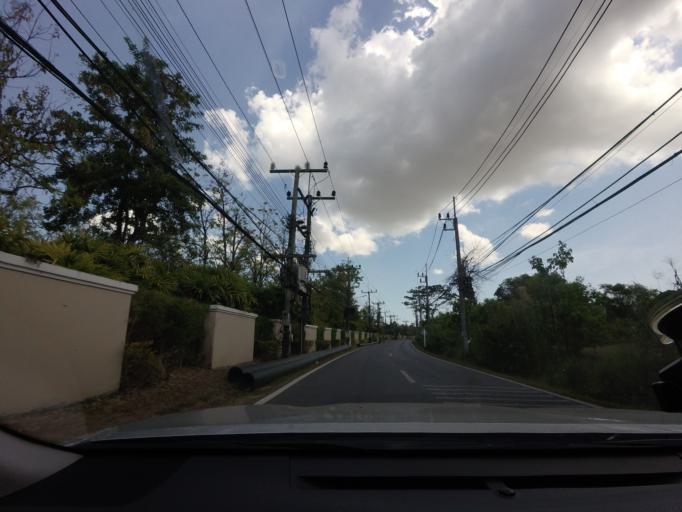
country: TH
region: Phuket
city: Thalang
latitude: 8.0193
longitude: 98.3027
